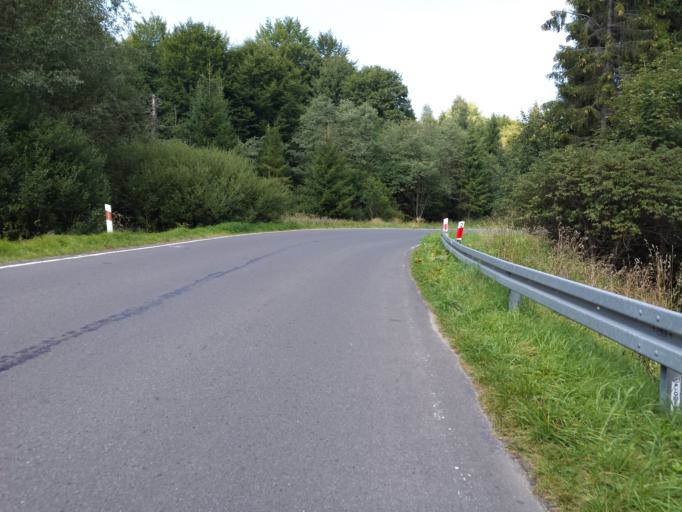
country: PL
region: Subcarpathian Voivodeship
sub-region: Powiat bieszczadzki
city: Lutowiska
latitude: 49.1051
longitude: 22.6290
